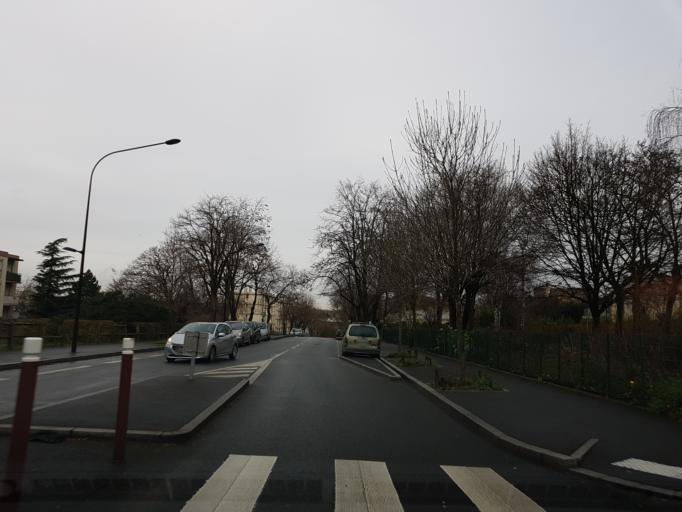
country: FR
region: Ile-de-France
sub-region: Departement du Val-de-Marne
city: L'Hay-les-Roses
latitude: 48.7888
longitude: 2.3370
